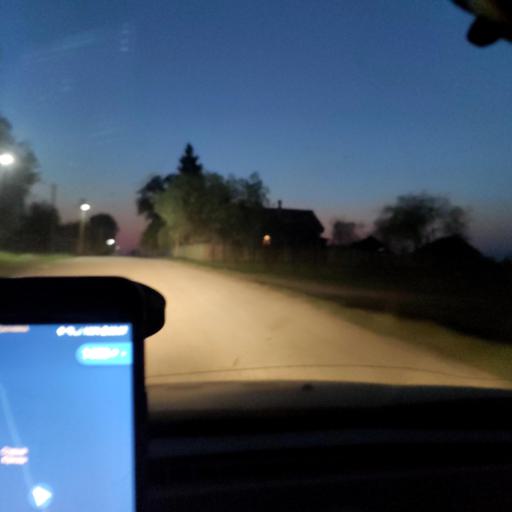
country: RU
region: Bashkortostan
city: Kabakovo
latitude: 54.6674
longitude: 56.2813
